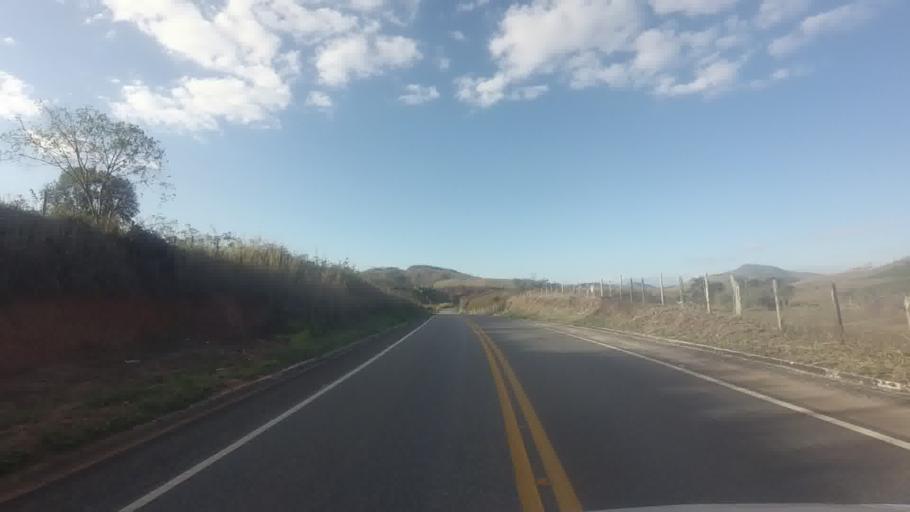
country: BR
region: Espirito Santo
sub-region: Jeronimo Monteiro
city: Jeronimo Monteiro
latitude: -20.9148
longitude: -41.3031
